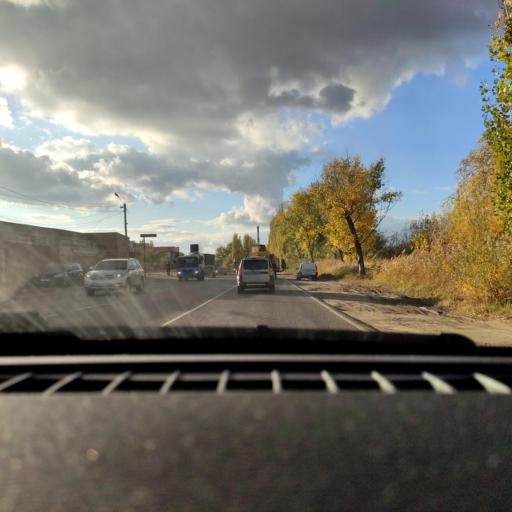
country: RU
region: Voronezj
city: Maslovka
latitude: 51.6222
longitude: 39.2508
